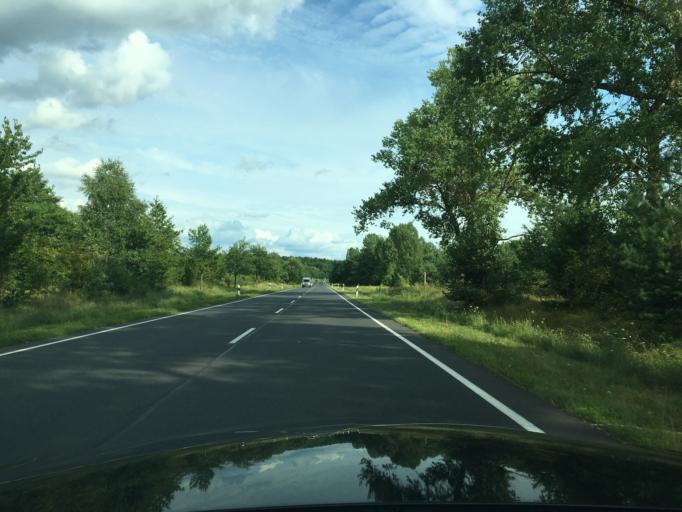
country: DE
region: Mecklenburg-Vorpommern
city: Neustrelitz
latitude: 53.3799
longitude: 13.0613
